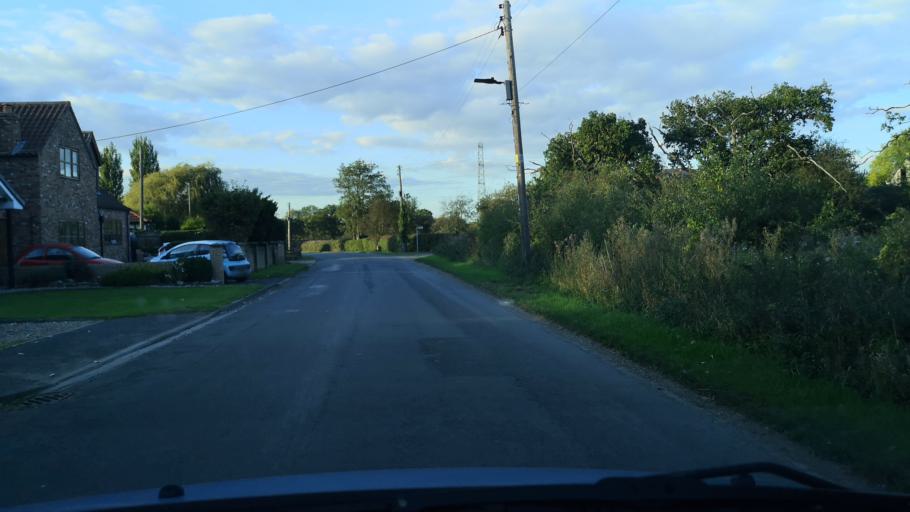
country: GB
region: England
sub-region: Doncaster
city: Stainforth
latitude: 53.6272
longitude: -1.0184
